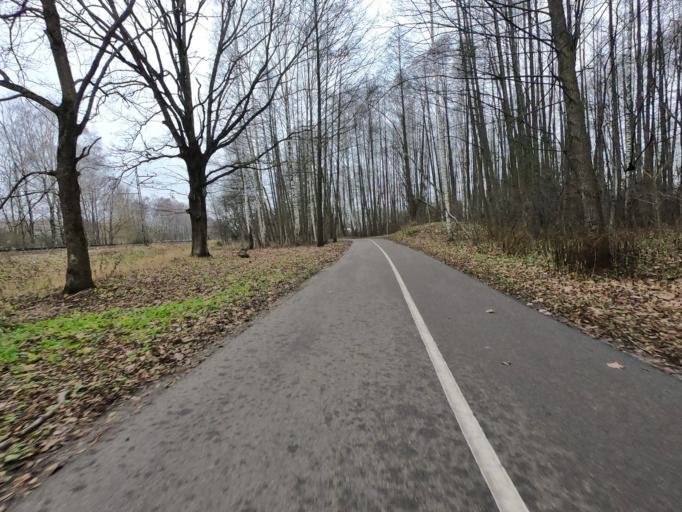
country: LV
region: Marupe
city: Marupe
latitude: 56.9502
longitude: 24.0126
